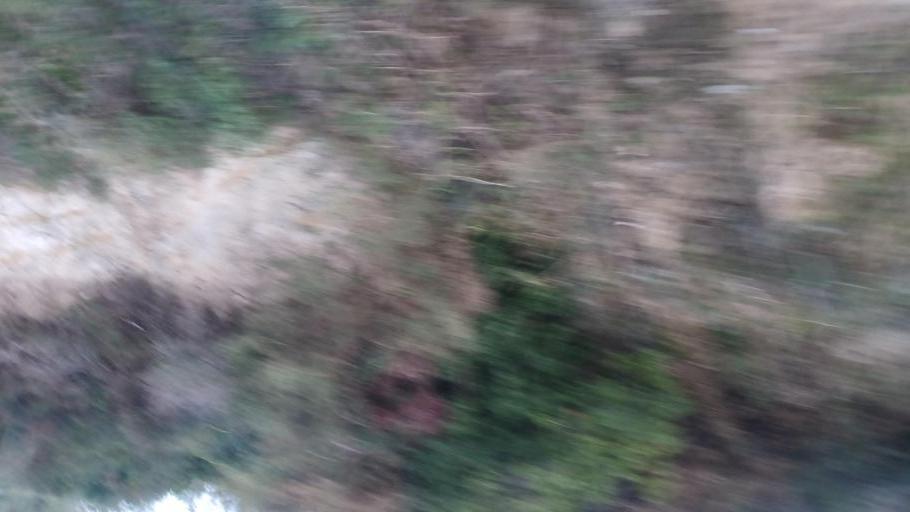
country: CY
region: Pafos
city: Polis
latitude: 34.9867
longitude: 32.4390
